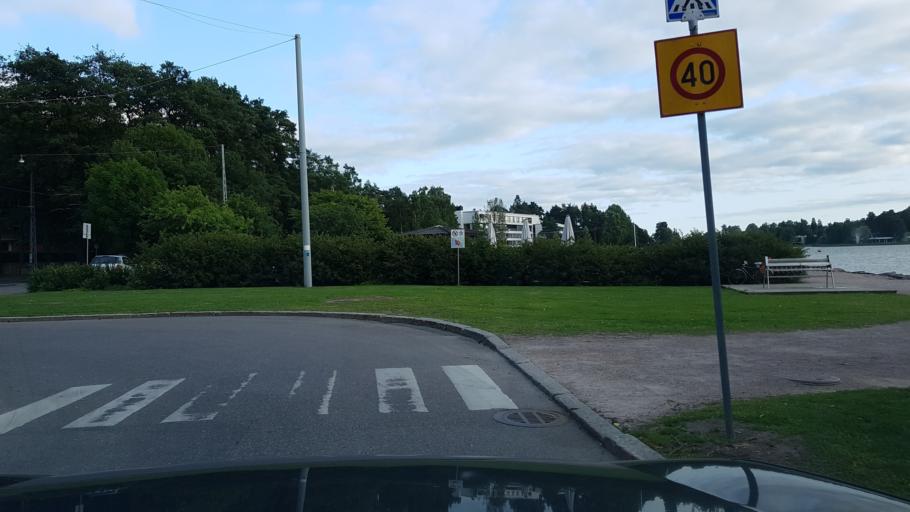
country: FI
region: Uusimaa
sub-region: Helsinki
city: Teekkarikylae
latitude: 60.1951
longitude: 24.8706
